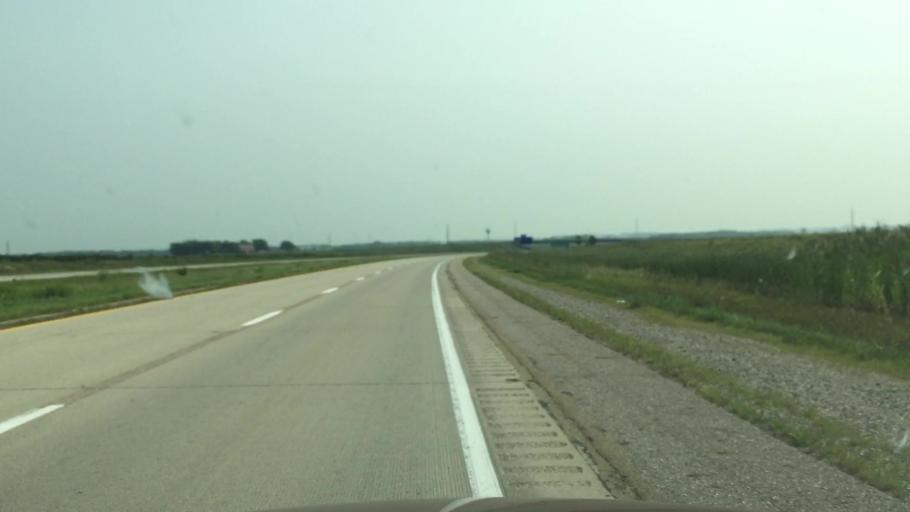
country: US
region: Iowa
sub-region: Osceola County
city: Sibley
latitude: 43.3781
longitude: -95.7575
